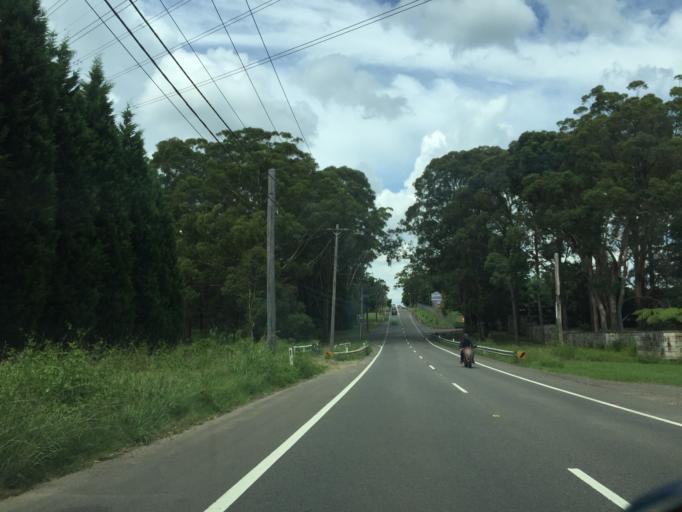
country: AU
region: New South Wales
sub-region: Hornsby Shire
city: Galston
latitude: -33.6733
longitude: 151.0346
